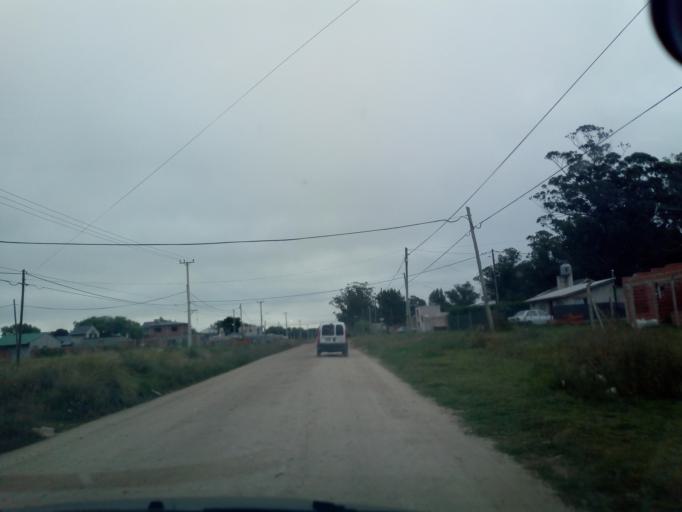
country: AR
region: Buenos Aires
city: Mar del Plata
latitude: -38.0657
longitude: -57.5673
